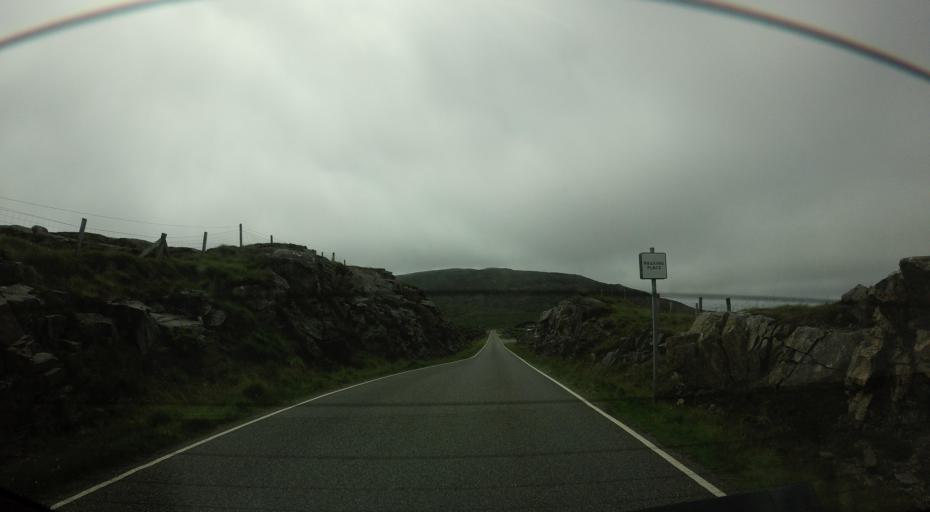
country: GB
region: Scotland
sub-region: Eilean Siar
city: Harris
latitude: 57.8672
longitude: -6.9140
